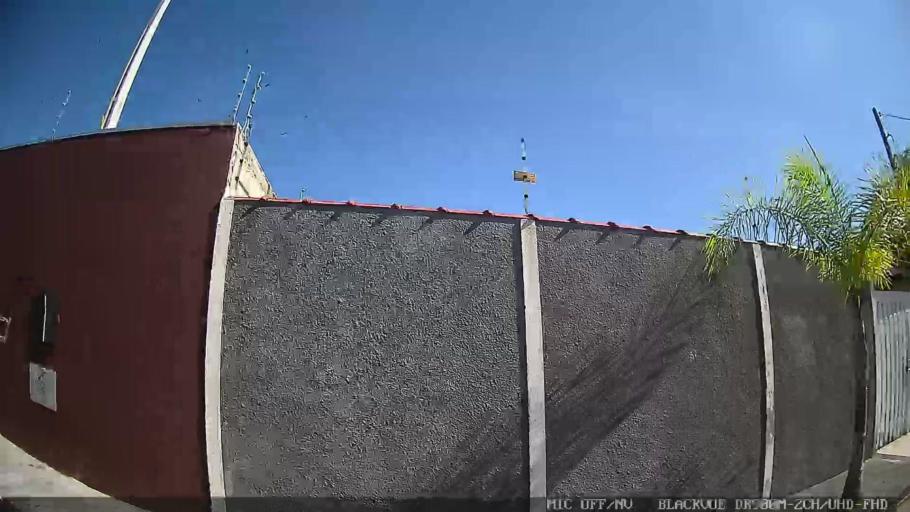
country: BR
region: Sao Paulo
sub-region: Peruibe
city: Peruibe
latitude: -24.2726
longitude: -46.9451
